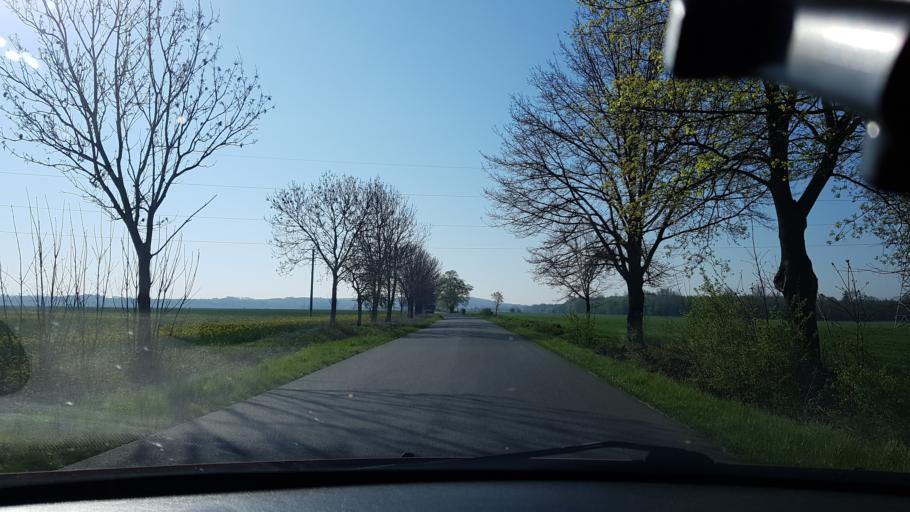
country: PL
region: Opole Voivodeship
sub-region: Powiat nyski
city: Nysa
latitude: 50.4281
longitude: 17.3072
